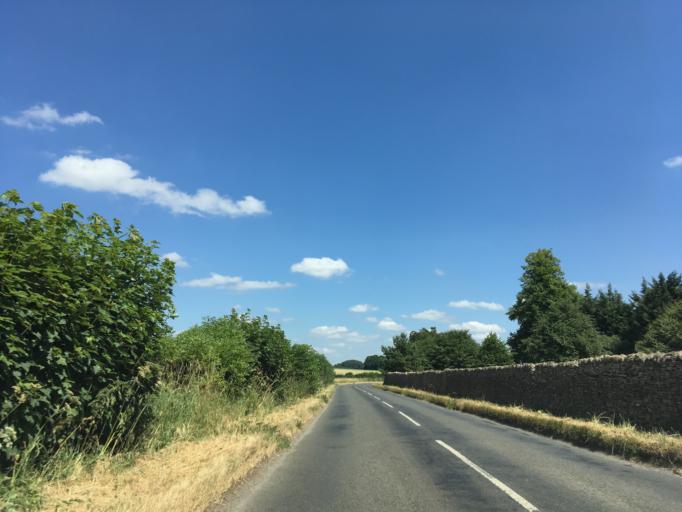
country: GB
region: England
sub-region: Gloucestershire
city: Chalford
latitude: 51.7554
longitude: -2.1662
